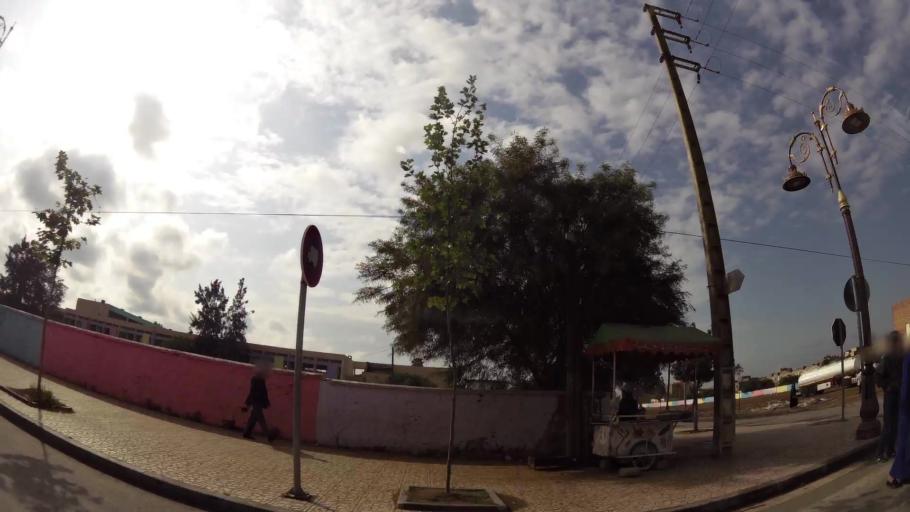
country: MA
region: Rabat-Sale-Zemmour-Zaer
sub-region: Khemisset
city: Tiflet
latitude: 33.8868
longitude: -6.3177
